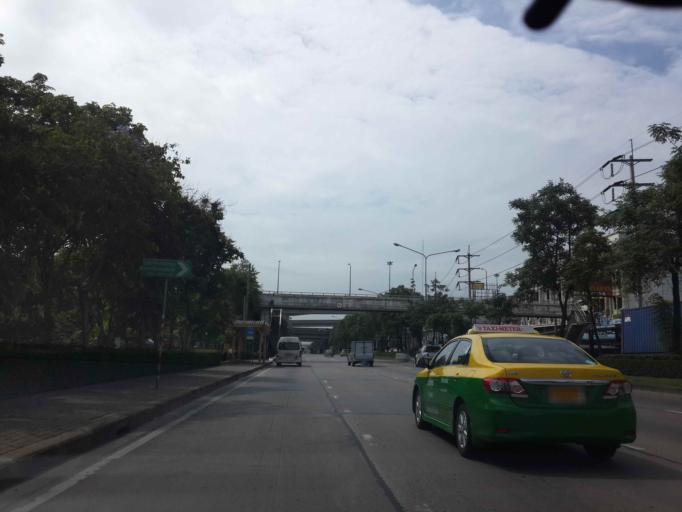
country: TH
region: Bangkok
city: Bang Khen
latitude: 13.8520
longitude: 100.6379
